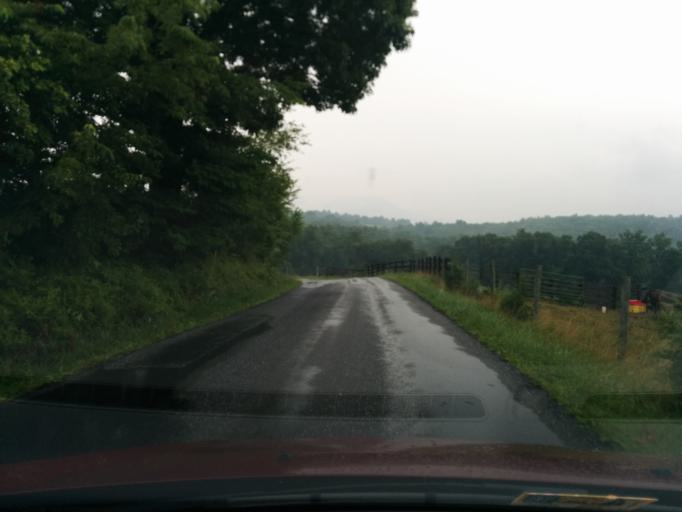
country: US
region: Virginia
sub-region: Rockbridge County
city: East Lexington
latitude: 37.8730
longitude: -79.4333
